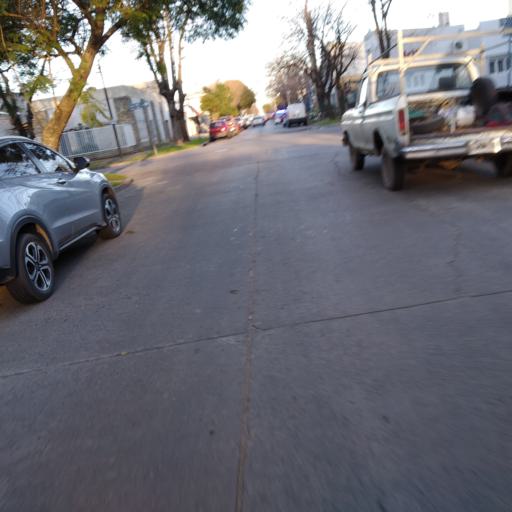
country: AR
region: Buenos Aires
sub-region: Partido de La Plata
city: La Plata
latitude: -34.9403
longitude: -57.9658
